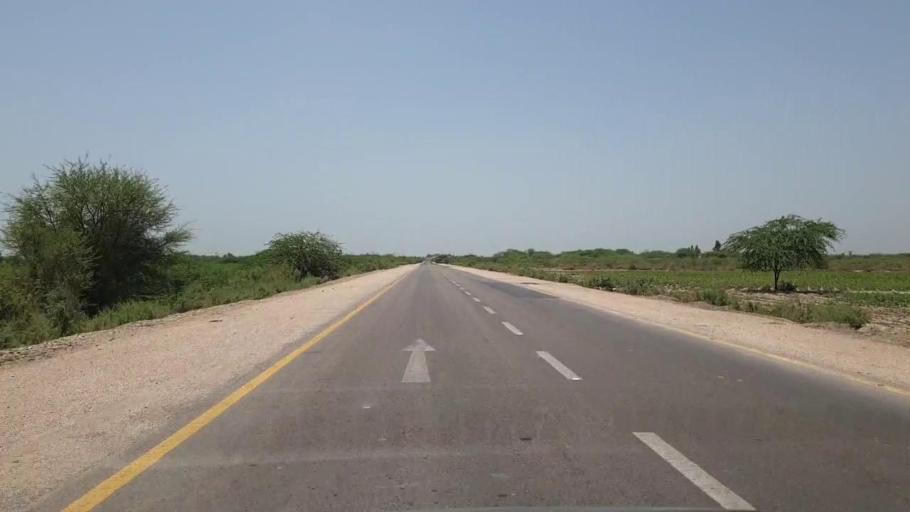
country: PK
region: Sindh
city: Sakrand
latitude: 26.1187
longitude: 68.3851
